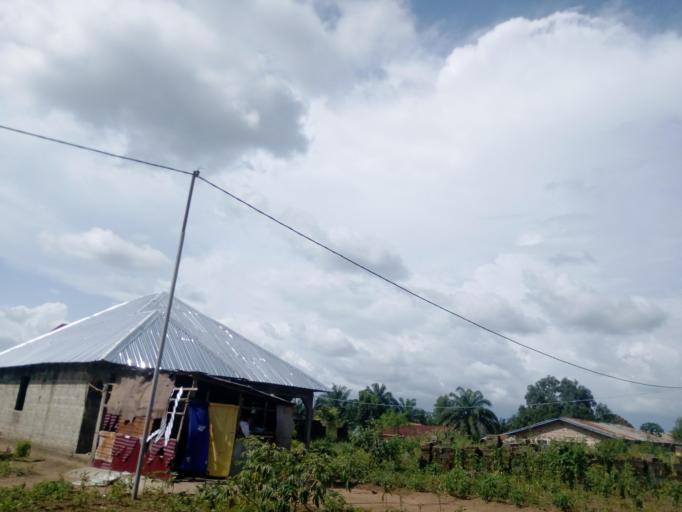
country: SL
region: Northern Province
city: Makeni
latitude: 8.9042
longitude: -12.0310
